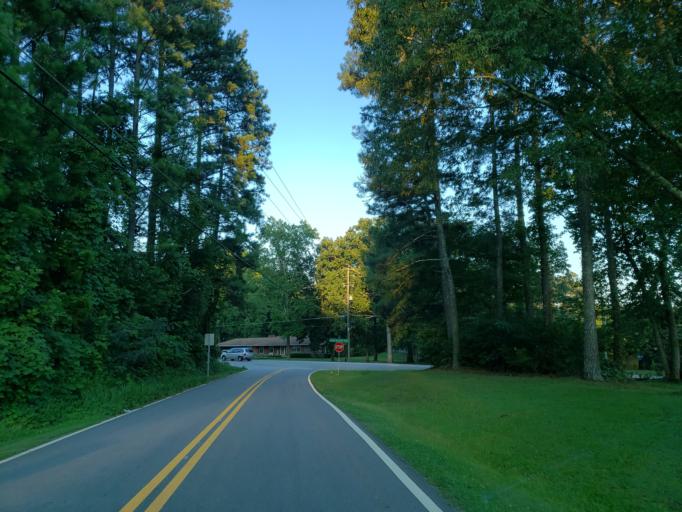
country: US
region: Georgia
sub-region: Paulding County
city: Dallas
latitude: 33.9921
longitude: -84.7681
